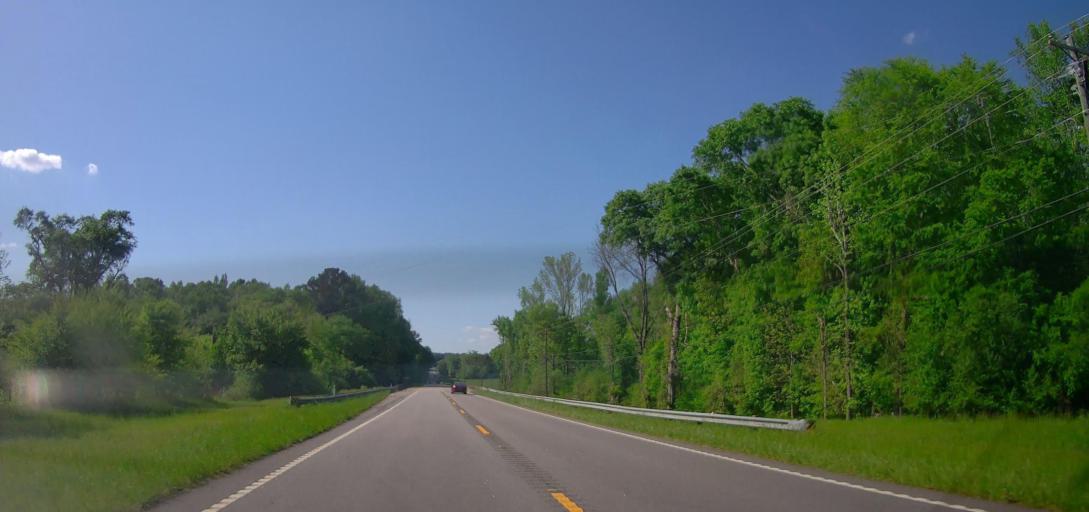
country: US
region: Georgia
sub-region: Morgan County
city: Madison
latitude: 33.6363
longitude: -83.4895
